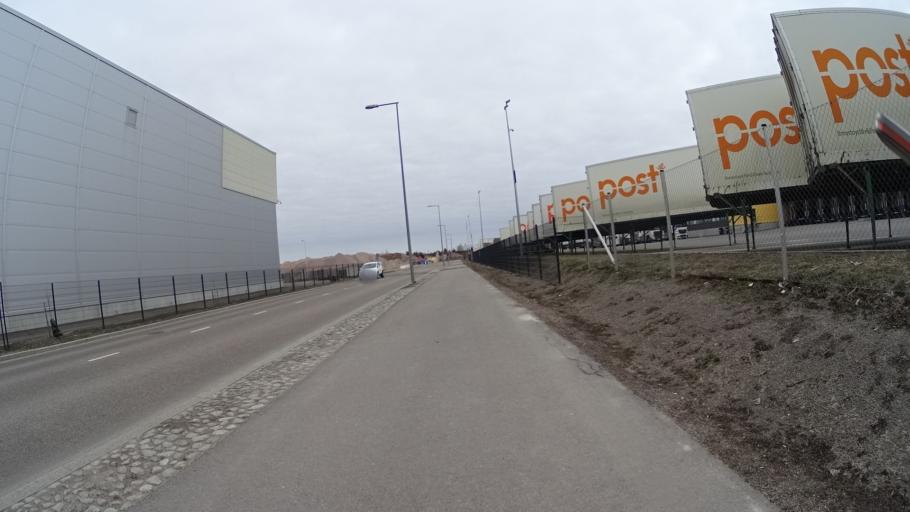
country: FI
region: Uusimaa
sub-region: Helsinki
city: Teekkarikylae
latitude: 60.3044
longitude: 24.8947
